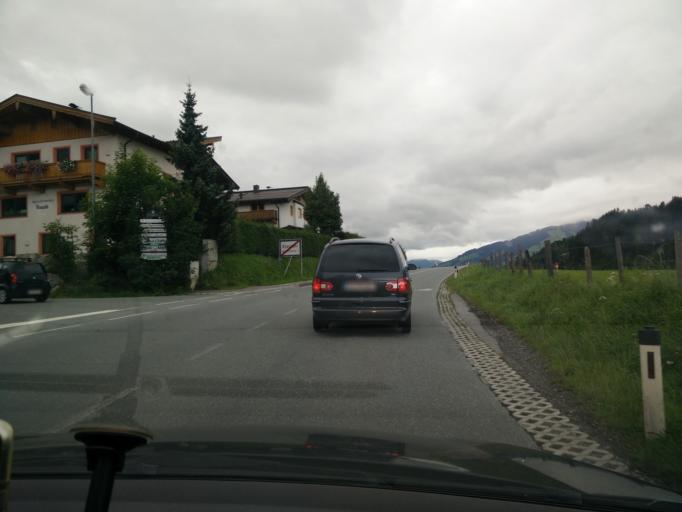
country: AT
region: Tyrol
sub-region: Politischer Bezirk Kitzbuhel
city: Kirchberg in Tirol
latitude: 47.4508
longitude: 12.3342
